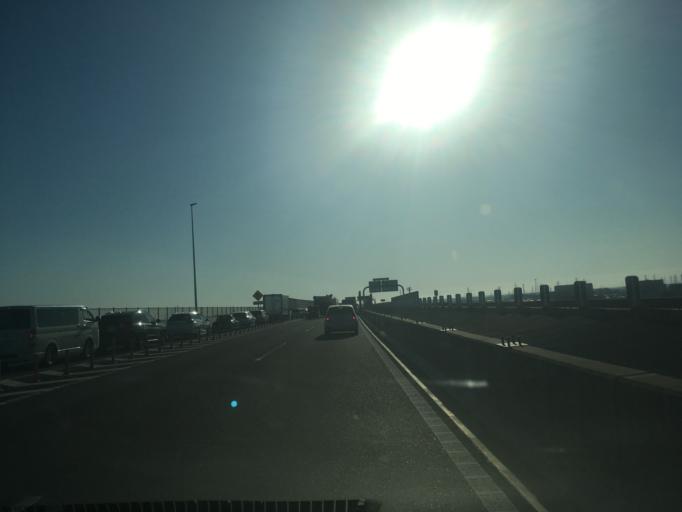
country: JP
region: Saitama
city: Kukichuo
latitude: 36.0467
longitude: 139.6664
